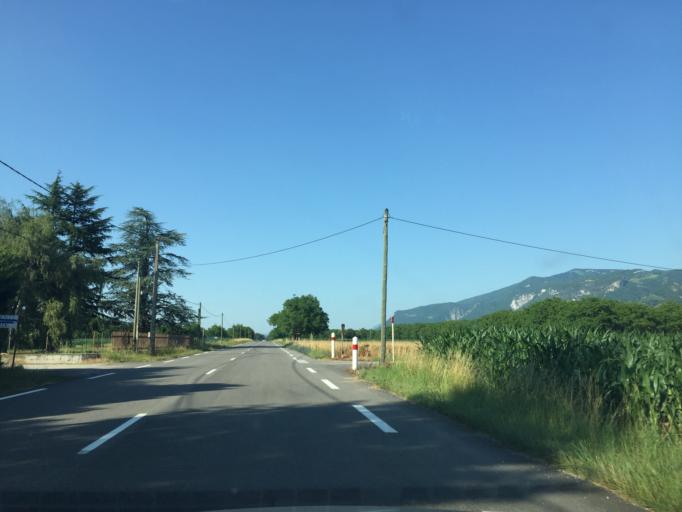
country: FR
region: Rhone-Alpes
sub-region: Departement de l'Isere
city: Saint-Just-de-Claix
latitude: 45.0949
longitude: 5.3037
